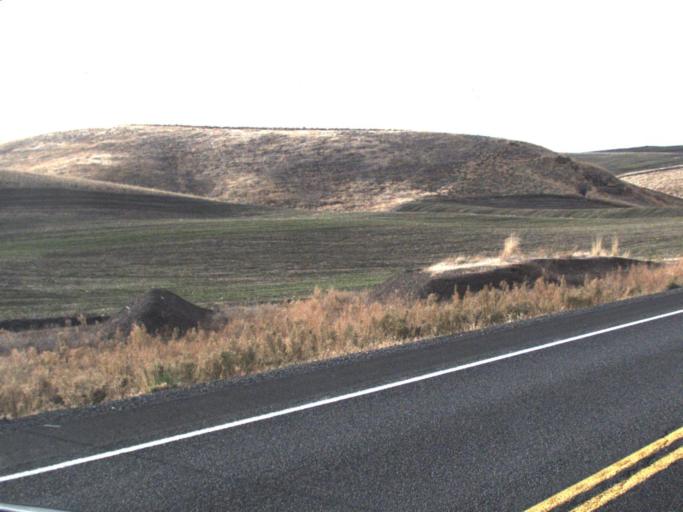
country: US
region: Washington
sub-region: Garfield County
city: Pomeroy
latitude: 46.5262
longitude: -117.8330
